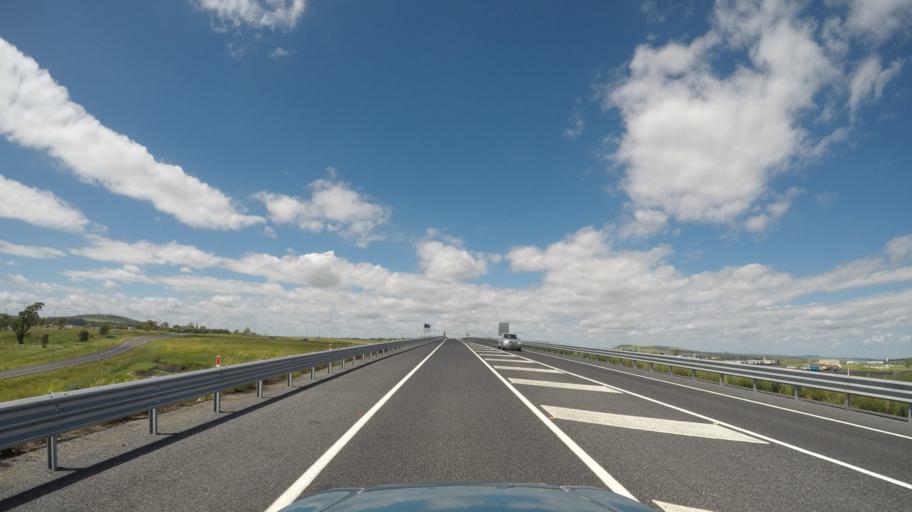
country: AU
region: Queensland
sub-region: Toowoomba
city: Wilsonton Heights
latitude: -27.5217
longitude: 151.8625
